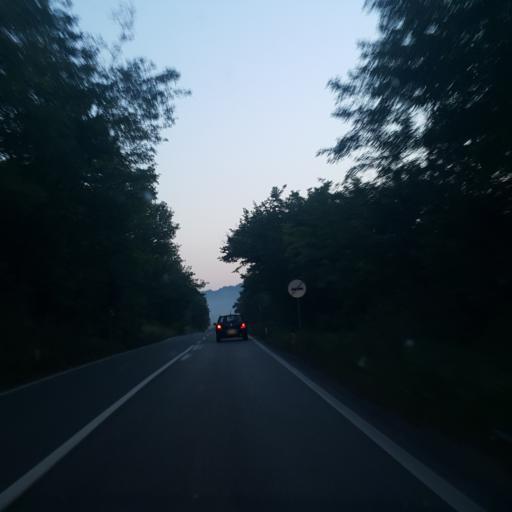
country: RS
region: Central Serbia
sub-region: Nisavski Okrug
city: Svrljig
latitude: 43.4242
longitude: 22.1327
